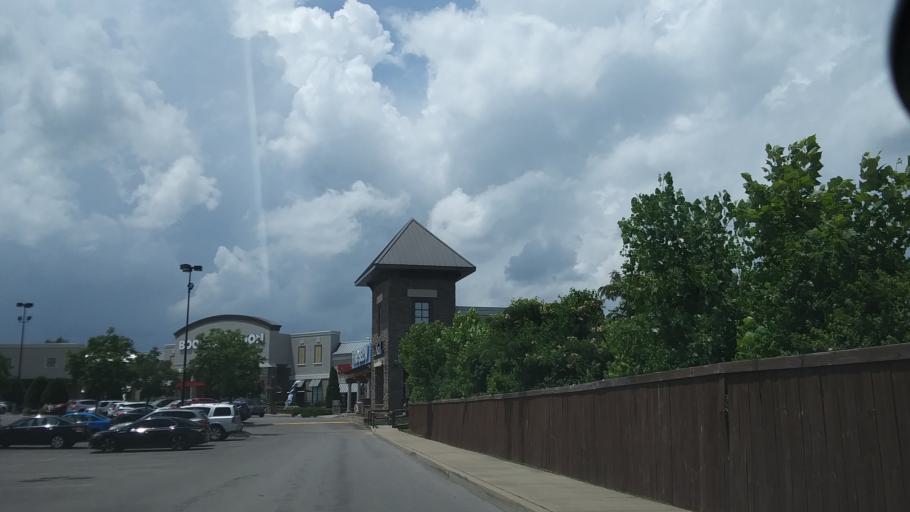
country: US
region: Tennessee
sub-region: Davidson County
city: Belle Meade
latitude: 36.1376
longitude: -86.8870
